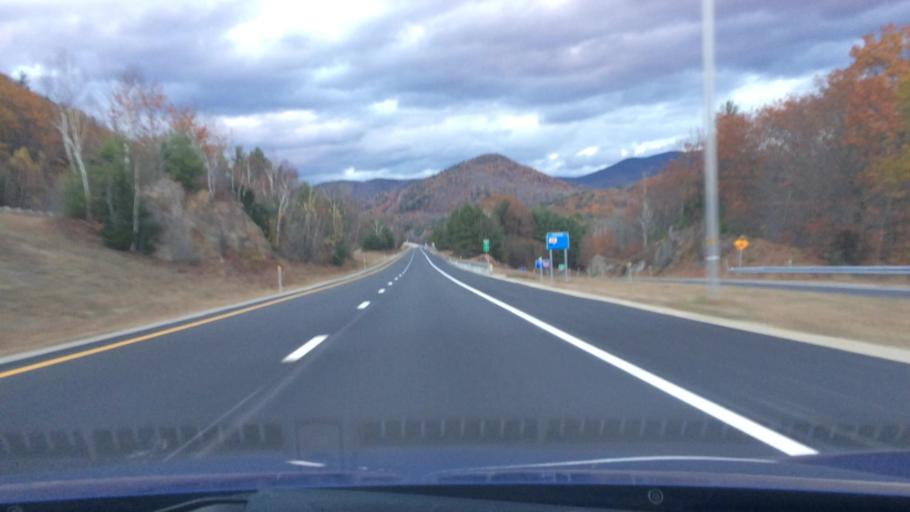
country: US
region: New Hampshire
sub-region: Grafton County
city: Woodstock
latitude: 43.9514
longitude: -71.6842
